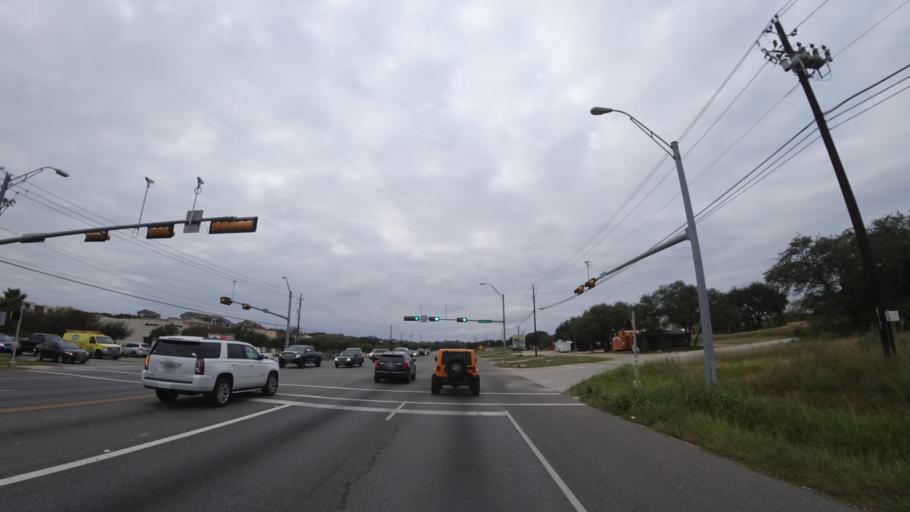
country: US
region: Texas
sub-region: Travis County
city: Bee Cave
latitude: 30.3197
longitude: -97.9523
